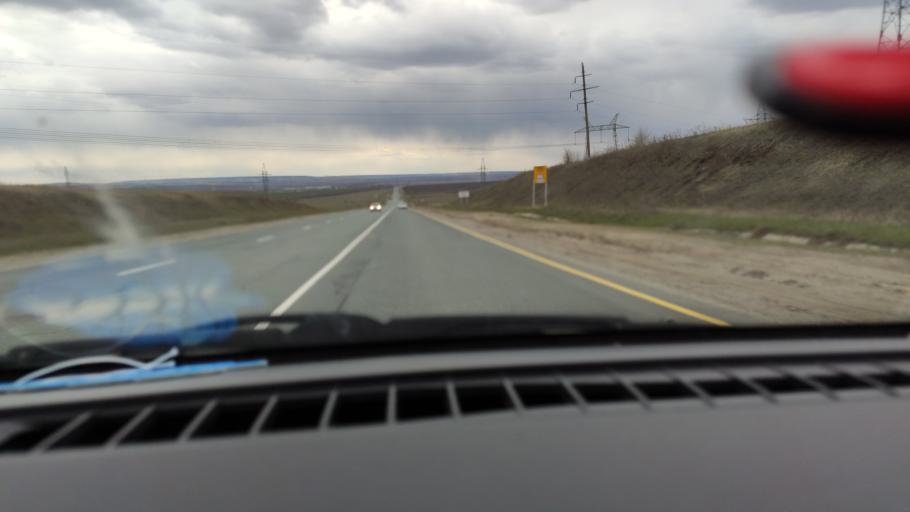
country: RU
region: Saratov
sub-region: Saratovskiy Rayon
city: Saratov
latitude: 51.7628
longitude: 46.0738
